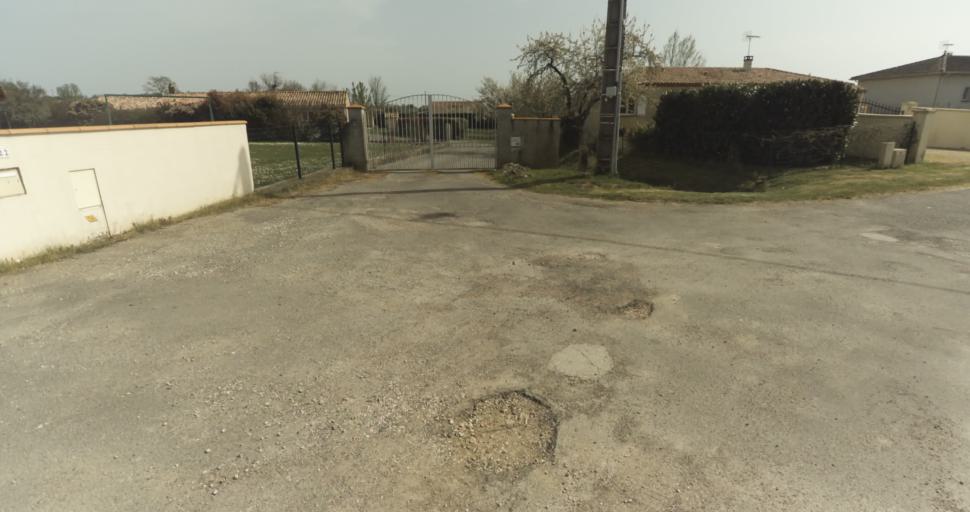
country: FR
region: Midi-Pyrenees
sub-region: Departement du Tarn-et-Garonne
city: Moissac
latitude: 44.1254
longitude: 1.1489
